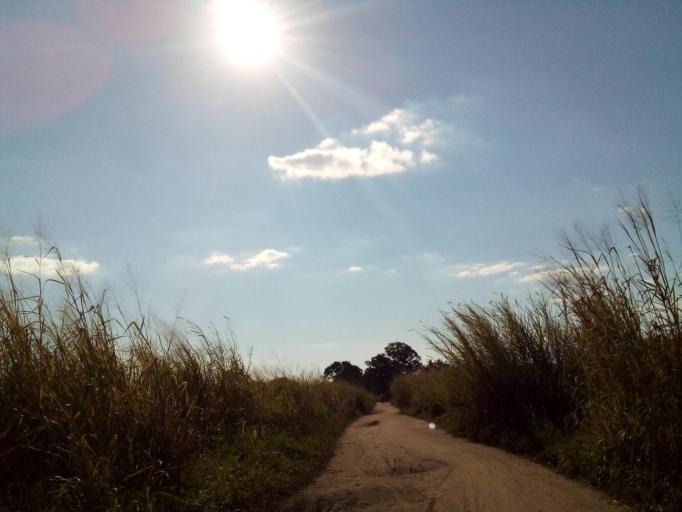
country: MZ
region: Zambezia
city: Quelimane
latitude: -17.5421
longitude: 36.6916
